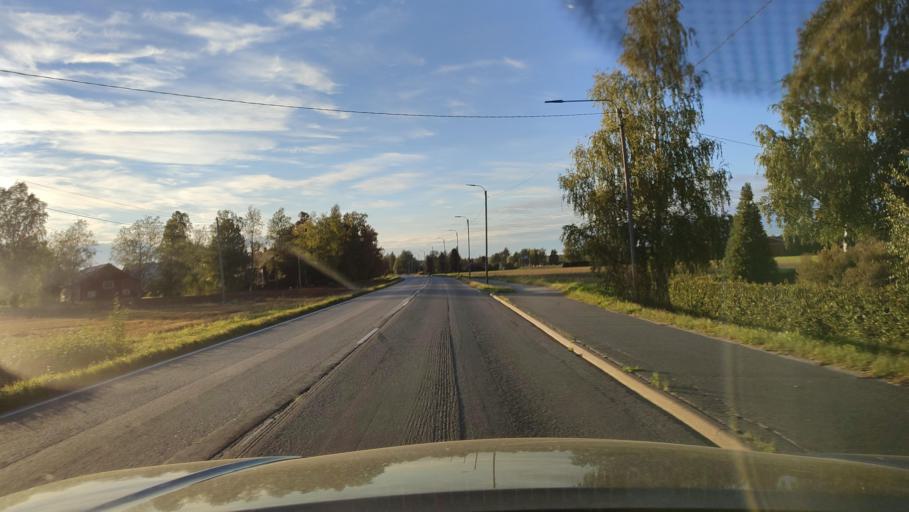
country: FI
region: Ostrobothnia
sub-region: Sydosterbotten
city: Kristinestad
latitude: 62.2568
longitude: 21.4979
